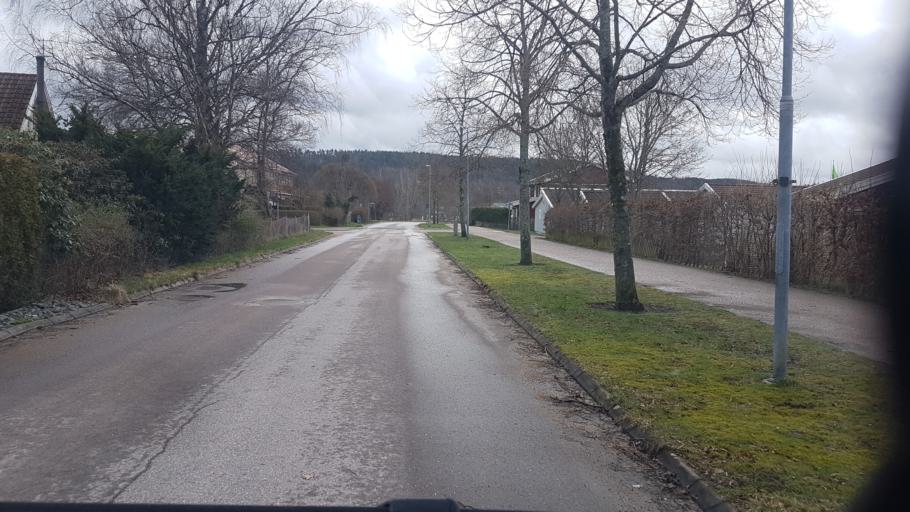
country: SE
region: Vaestra Goetaland
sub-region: Lerums Kommun
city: Stenkullen
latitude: 57.7878
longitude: 12.3027
